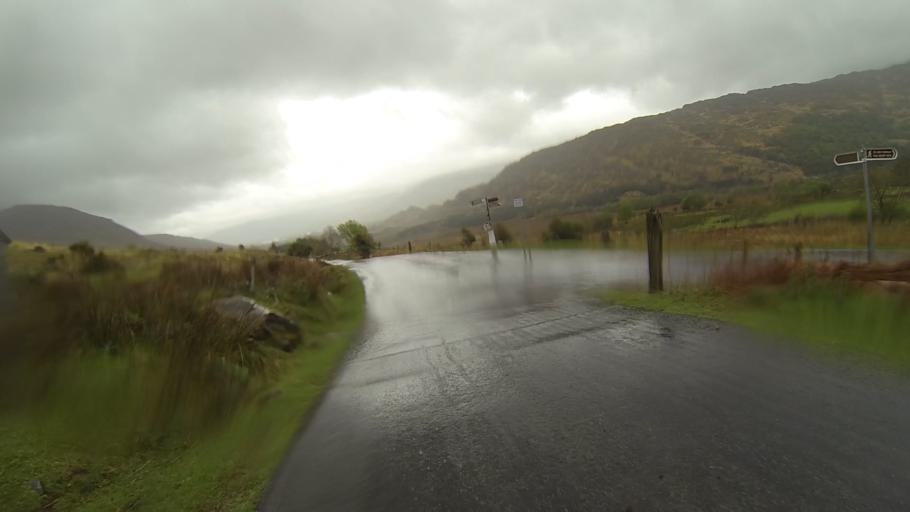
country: IE
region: Munster
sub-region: Ciarrai
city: Kenmare
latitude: 51.9875
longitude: -9.6598
